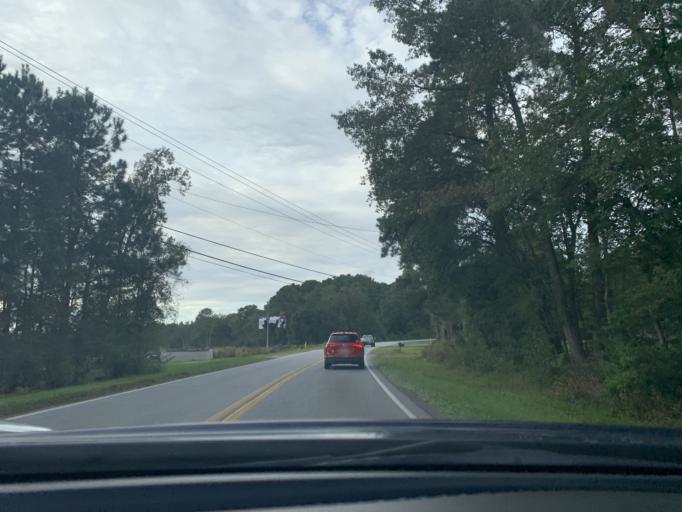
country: US
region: Georgia
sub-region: Chatham County
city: Georgetown
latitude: 32.0381
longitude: -81.2596
